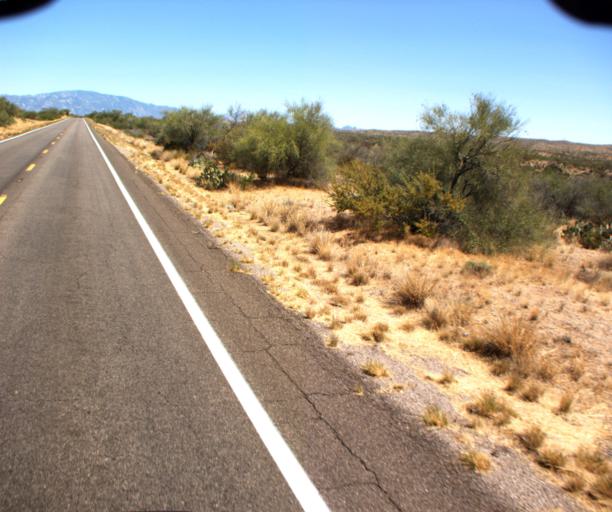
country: US
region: Arizona
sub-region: Pima County
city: Catalina
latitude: 32.6391
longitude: -111.0127
